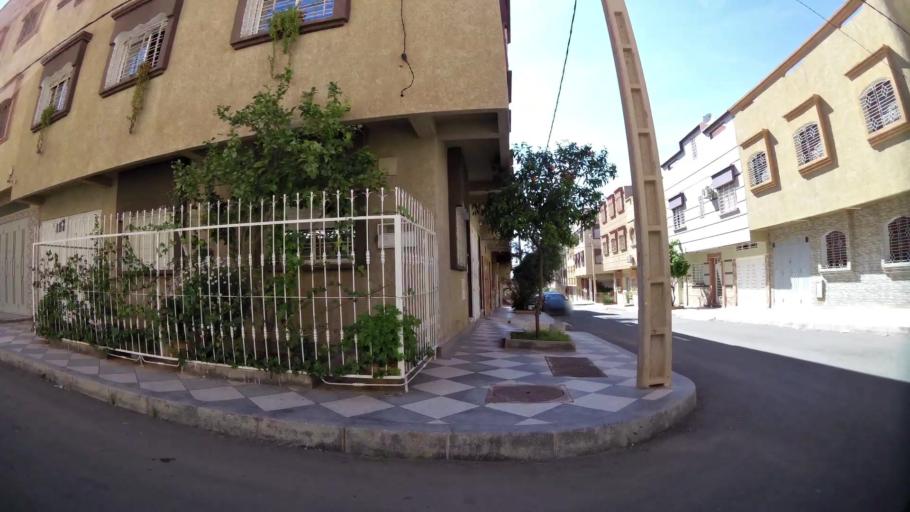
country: MA
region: Oriental
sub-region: Oujda-Angad
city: Oujda
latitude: 34.6594
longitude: -1.9180
